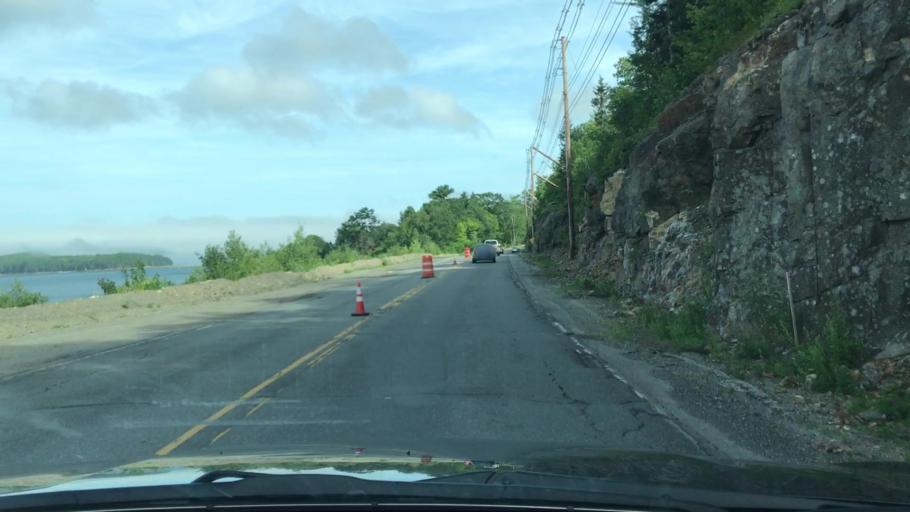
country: US
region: Maine
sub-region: Hancock County
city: Bar Harbor
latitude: 44.4069
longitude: -68.2369
